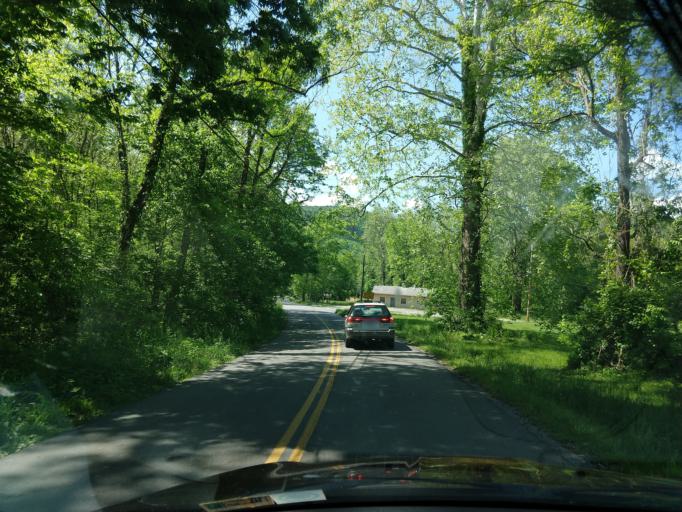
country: US
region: Virginia
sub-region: City of Covington
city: Fairlawn
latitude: 37.6915
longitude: -79.8892
